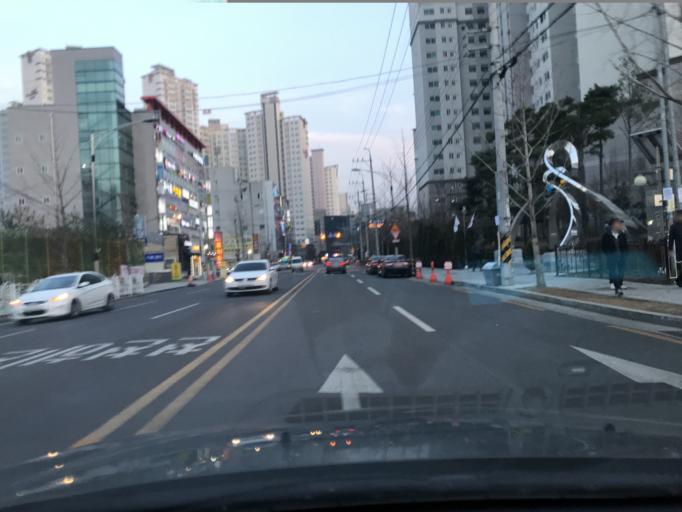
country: KR
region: Daegu
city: Hwawon
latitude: 35.8163
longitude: 128.5185
